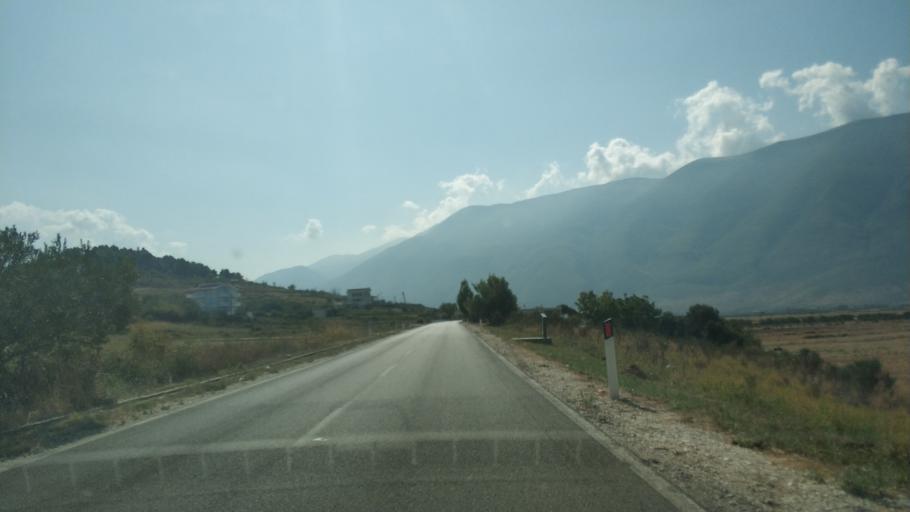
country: AL
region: Vlore
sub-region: Rrethi i Vlores
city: Orikum
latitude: 40.3082
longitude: 19.4812
